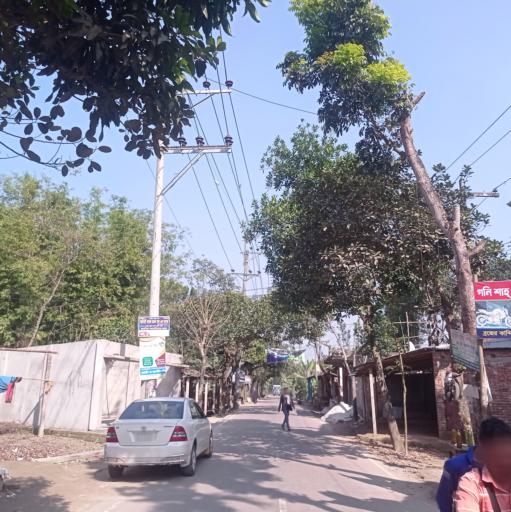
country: BD
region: Dhaka
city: Narsingdi
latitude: 24.0257
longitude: 90.6702
